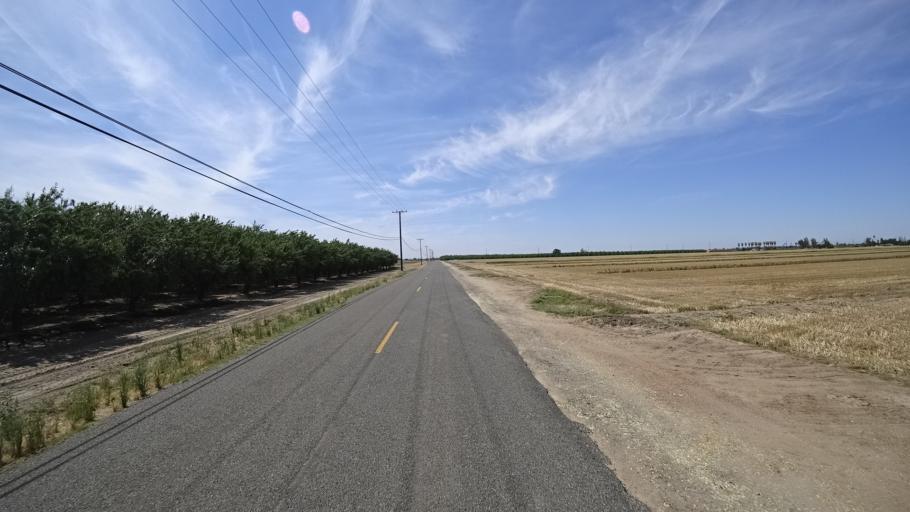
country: US
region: California
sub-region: Kings County
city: Hanford
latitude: 36.3474
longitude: -119.6101
